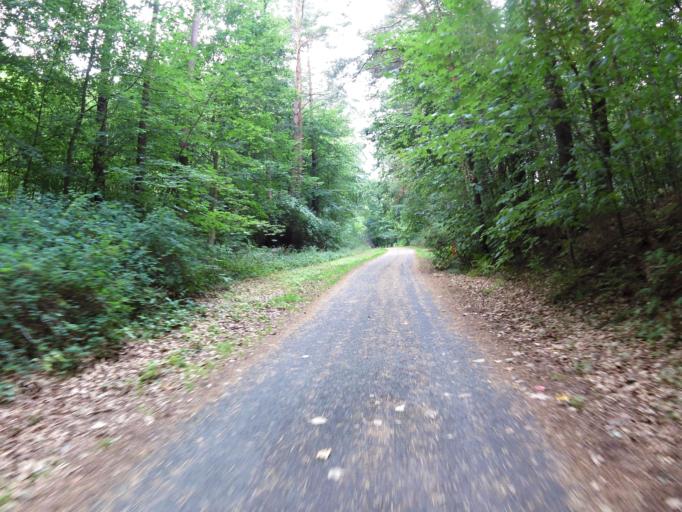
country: DE
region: Mecklenburg-Vorpommern
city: Seebad Heringsdorf
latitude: 53.9299
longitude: 14.1802
